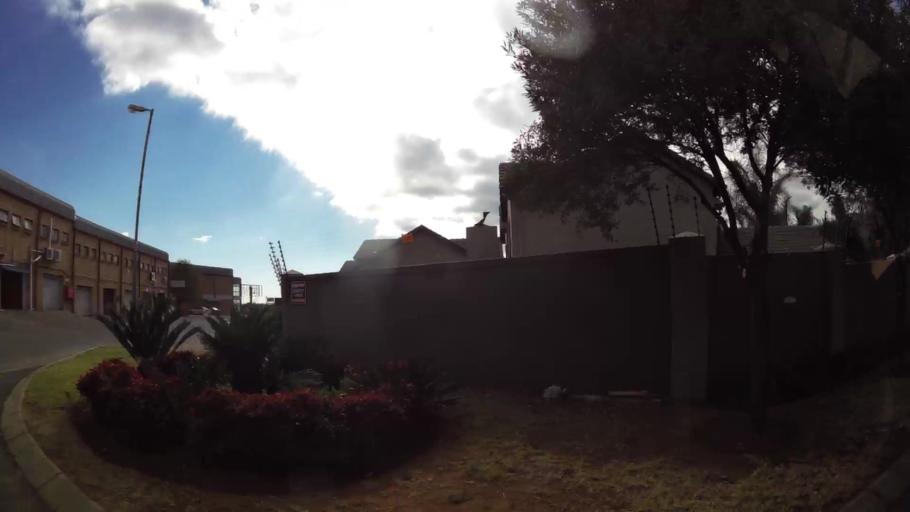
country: ZA
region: Gauteng
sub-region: West Rand District Municipality
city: Muldersdriseloop
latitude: -26.0942
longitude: 27.8698
